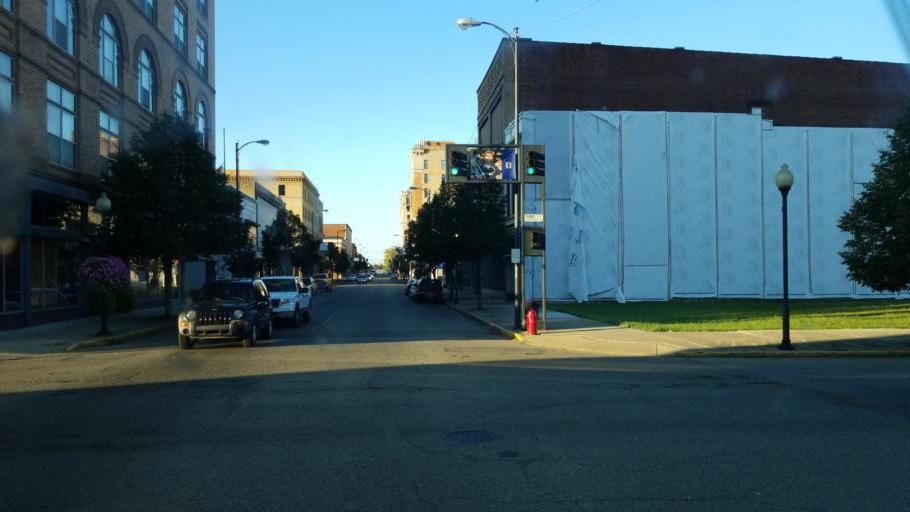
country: US
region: Ohio
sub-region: Scioto County
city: Portsmouth
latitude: 38.7322
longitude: -82.9966
